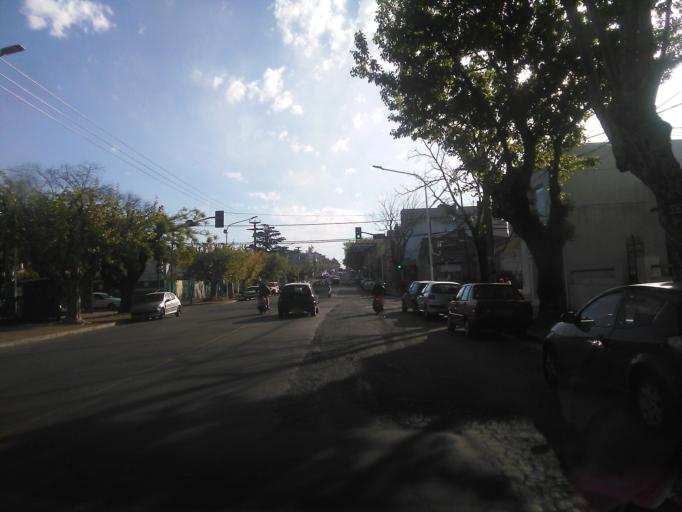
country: AR
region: Buenos Aires
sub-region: Partido de Tandil
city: Tandil
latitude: -37.3328
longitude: -59.1305
